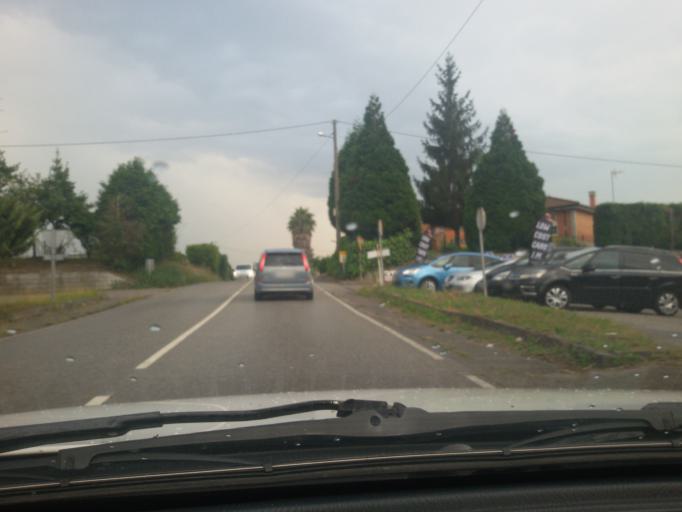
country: ES
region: Asturias
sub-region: Province of Asturias
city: Lugones
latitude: 43.3984
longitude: -5.7906
